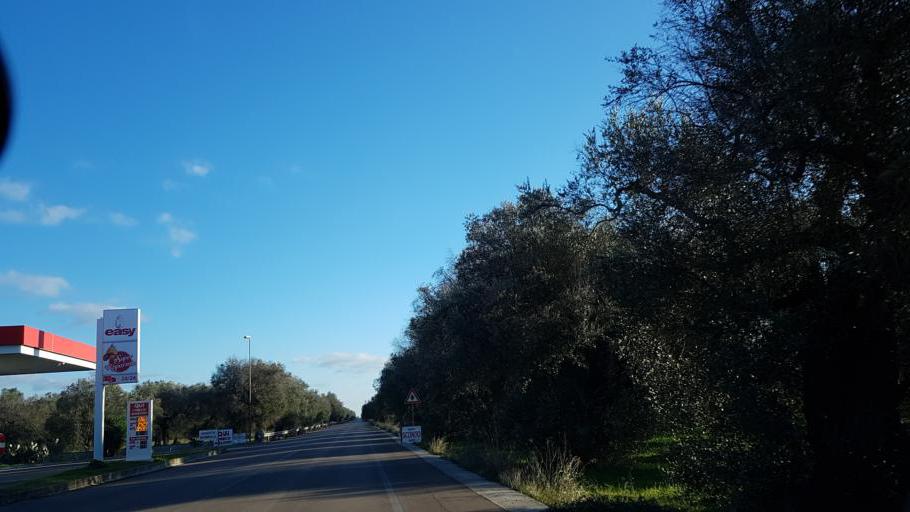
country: IT
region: Apulia
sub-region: Provincia di Brindisi
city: San Pietro Vernotico
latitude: 40.4718
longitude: 18.0118
